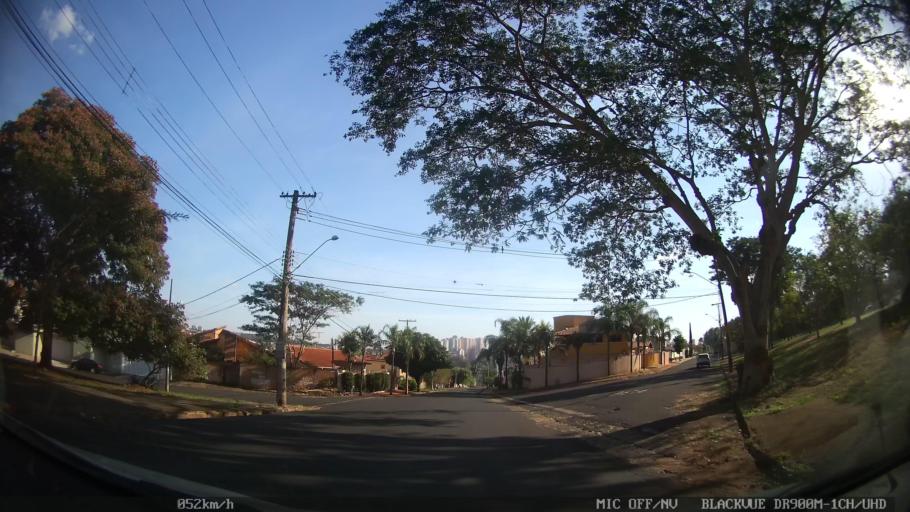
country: BR
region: Sao Paulo
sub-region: Ribeirao Preto
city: Ribeirao Preto
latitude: -21.2057
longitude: -47.7797
